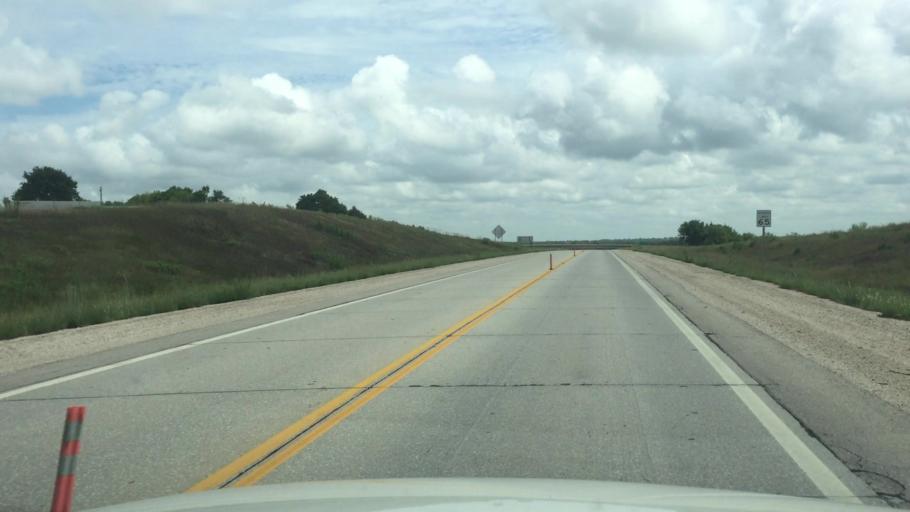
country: US
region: Kansas
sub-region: Allen County
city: Iola
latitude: 37.8875
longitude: -95.3905
